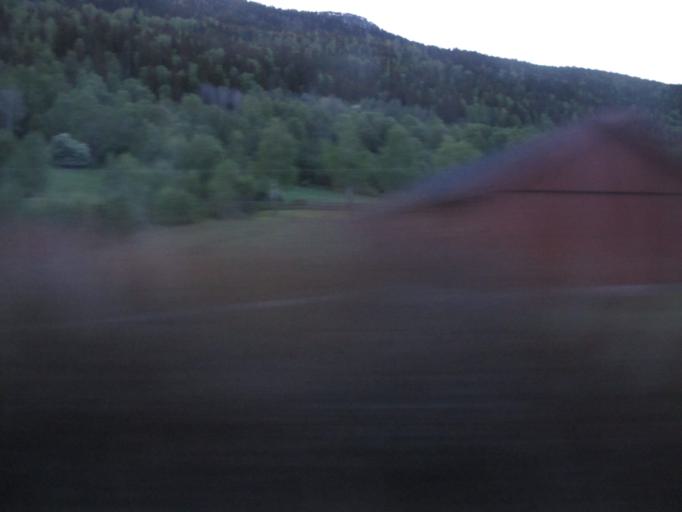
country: NO
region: Oppland
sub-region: Nord-Fron
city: Vinstra
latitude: 61.5818
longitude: 9.8413
